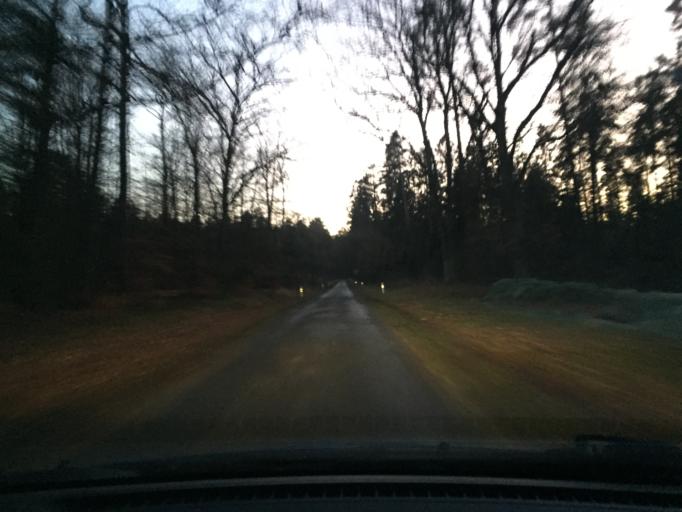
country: DE
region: Lower Saxony
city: Gohrde
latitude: 53.1761
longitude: 10.9188
